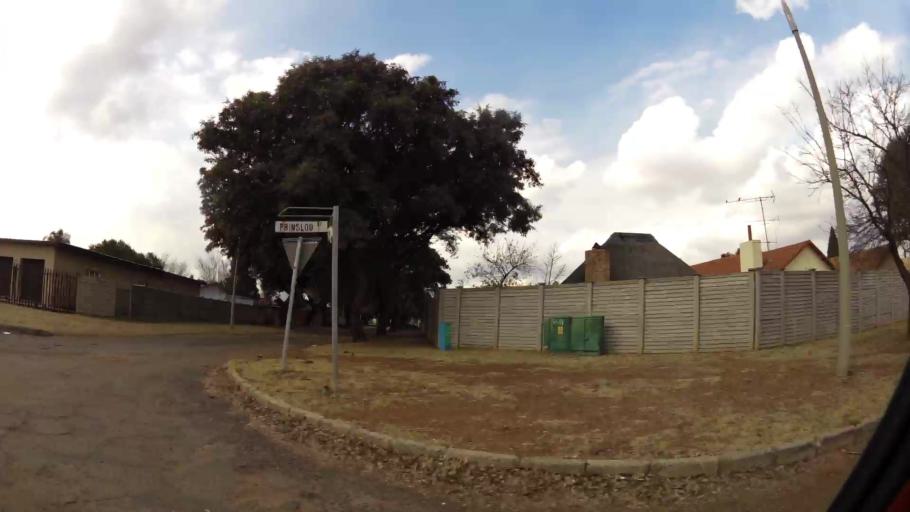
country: ZA
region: Gauteng
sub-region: Sedibeng District Municipality
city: Vanderbijlpark
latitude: -26.7227
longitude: 27.8489
